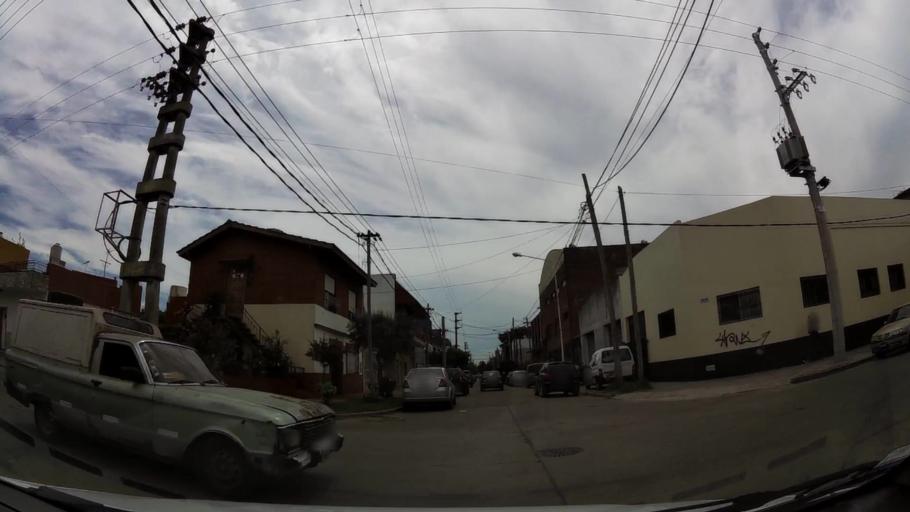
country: AR
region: Buenos Aires
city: San Justo
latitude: -34.6741
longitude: -58.5348
